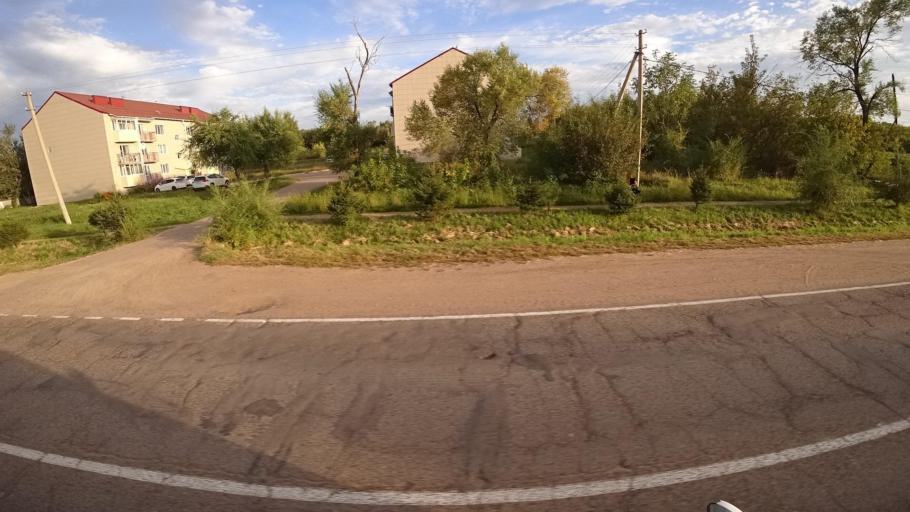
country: RU
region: Primorskiy
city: Yakovlevka
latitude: 44.4256
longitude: 133.4707
